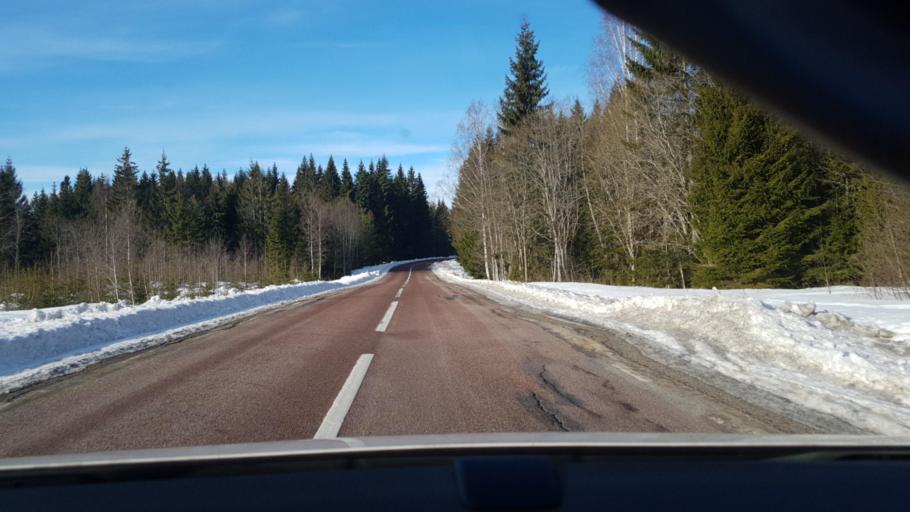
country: SE
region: Vaermland
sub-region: Eda Kommun
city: Amotfors
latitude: 59.7643
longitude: 12.2394
